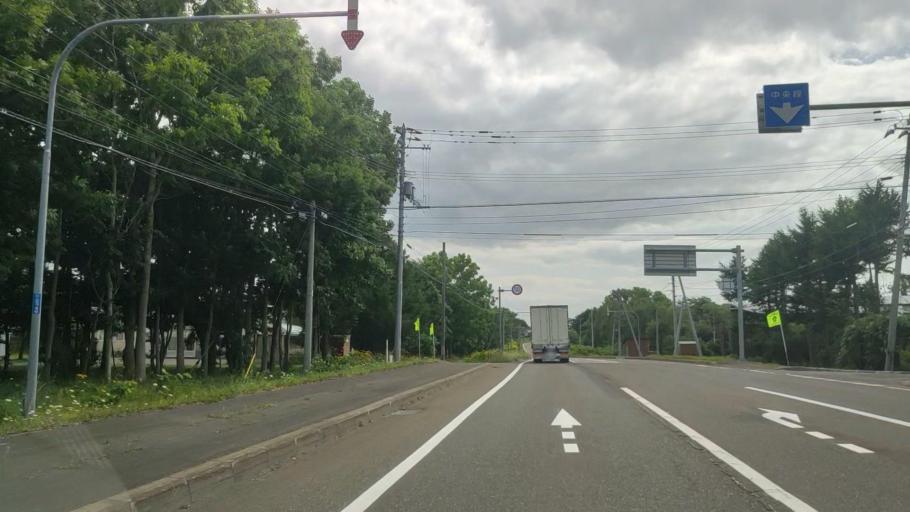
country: JP
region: Hokkaido
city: Rumoi
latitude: 44.5626
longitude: 141.7858
